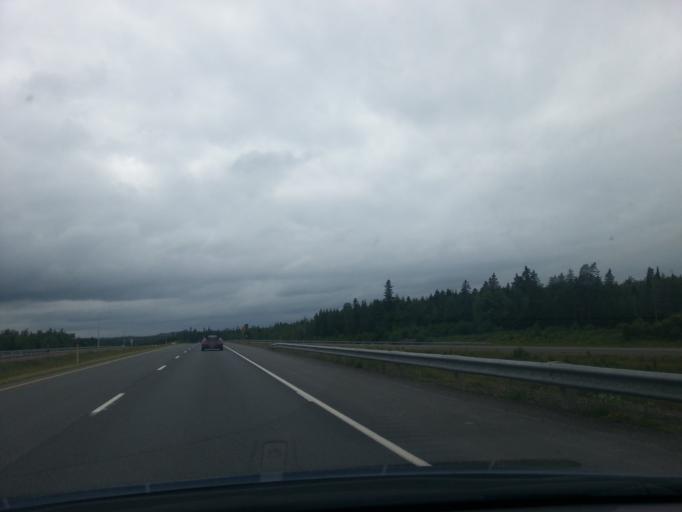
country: US
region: Maine
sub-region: Aroostook County
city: Limestone
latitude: 46.9759
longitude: -67.7312
